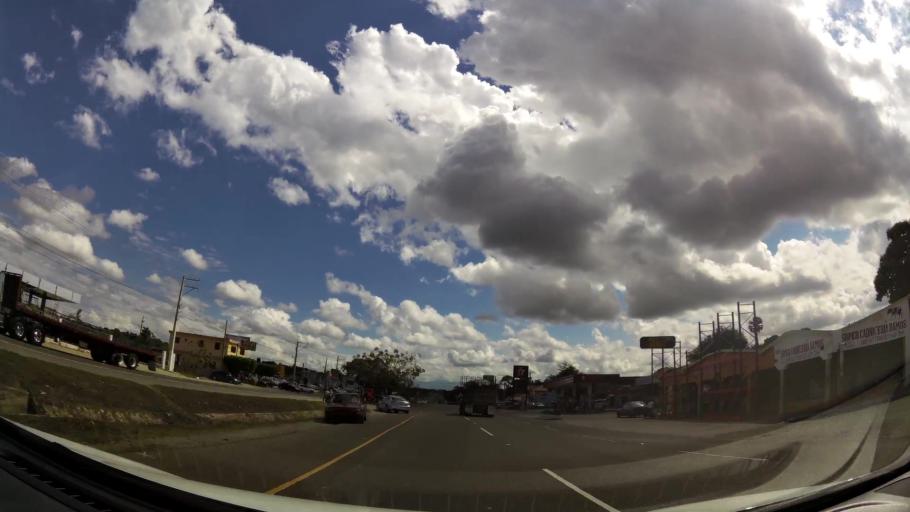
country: DO
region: La Vega
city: Rio Verde Arriba
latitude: 19.3669
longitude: -70.6032
